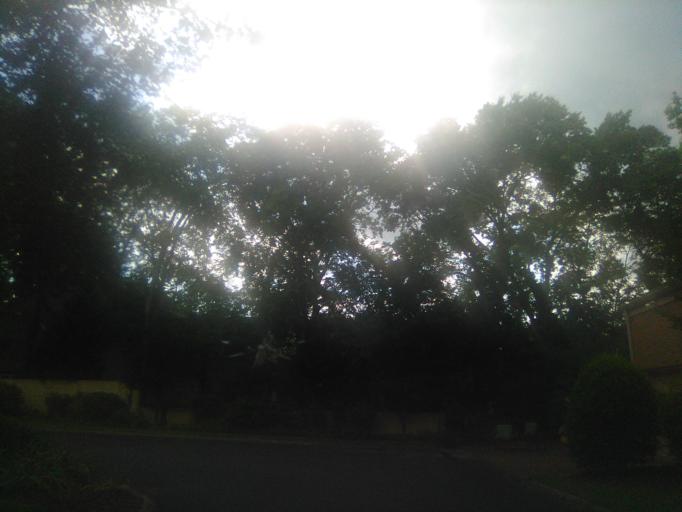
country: US
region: Tennessee
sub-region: Davidson County
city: Belle Meade
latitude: 36.1006
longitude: -86.8320
